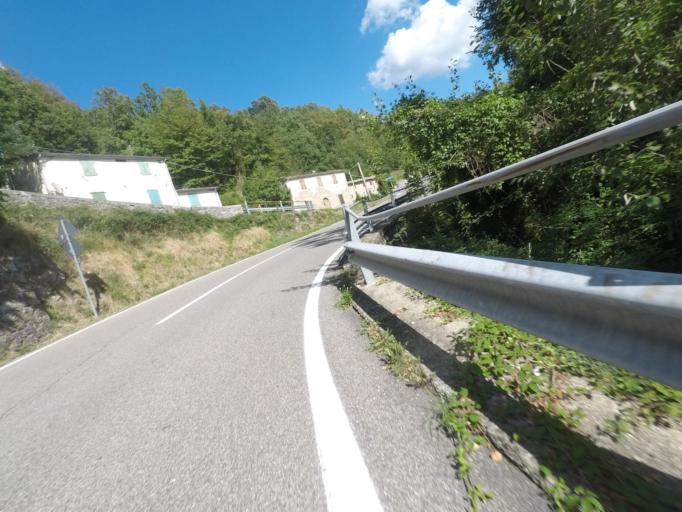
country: IT
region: Tuscany
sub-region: Provincia di Massa-Carrara
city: Fivizzano
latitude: 44.2596
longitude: 10.1785
